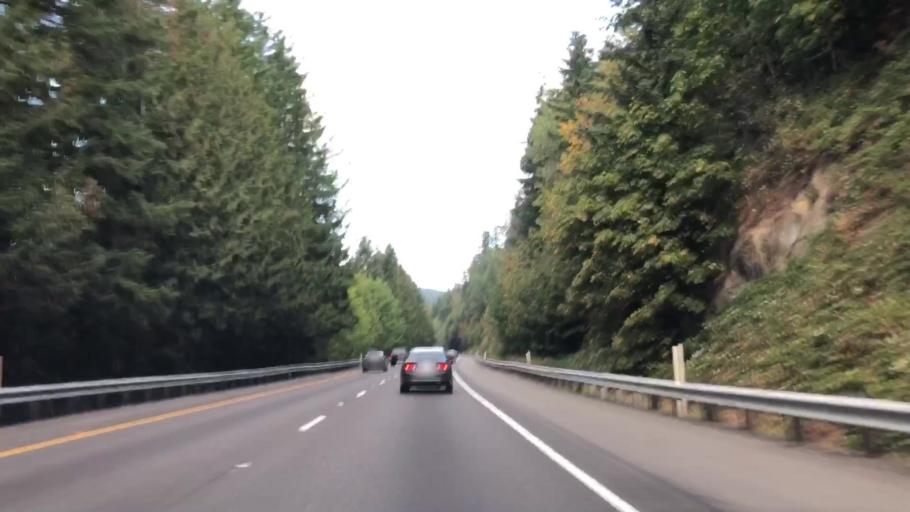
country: US
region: Washington
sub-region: Whatcom County
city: Sudden Valley
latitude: 48.6702
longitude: -122.3795
